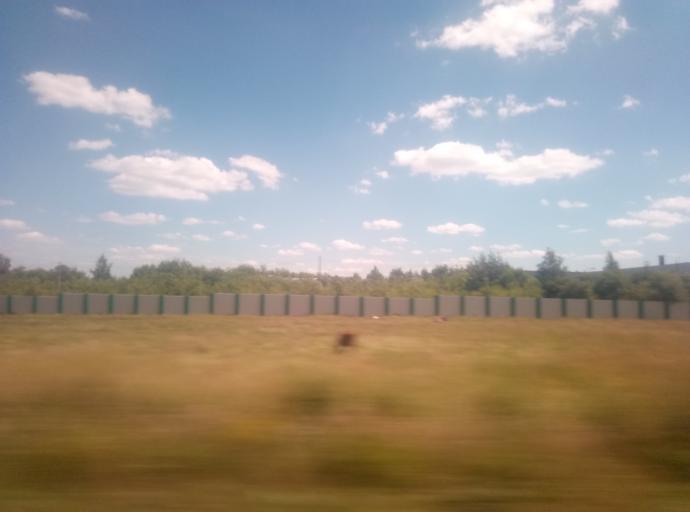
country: RU
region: Tula
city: Kireyevsk
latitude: 53.9607
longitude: 37.9378
